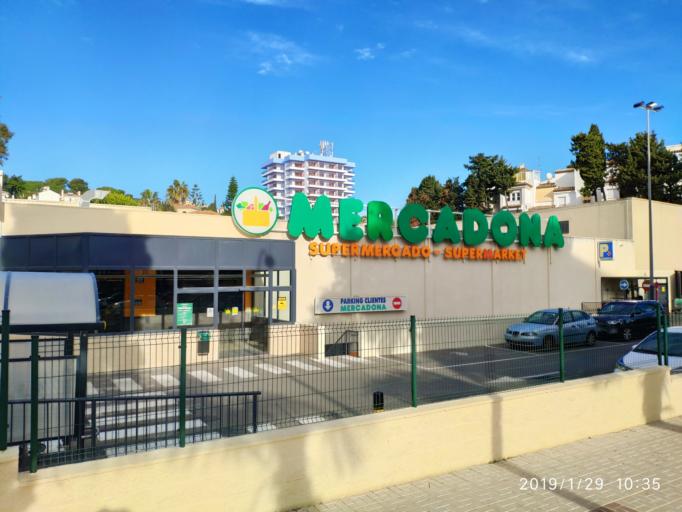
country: ES
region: Andalusia
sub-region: Provincia de Malaga
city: Torremolinos
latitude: 36.6073
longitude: -4.5096
